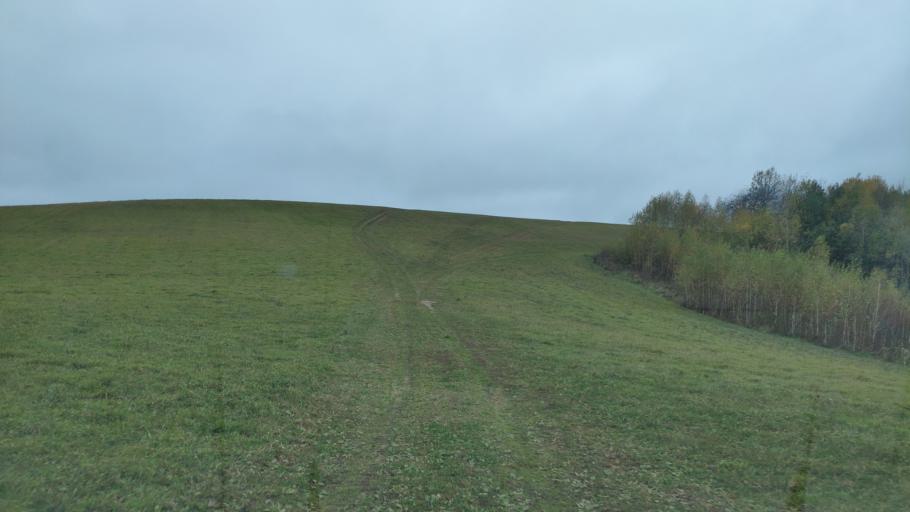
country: SK
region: Presovsky
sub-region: Okres Presov
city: Presov
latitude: 48.9361
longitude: 21.1219
